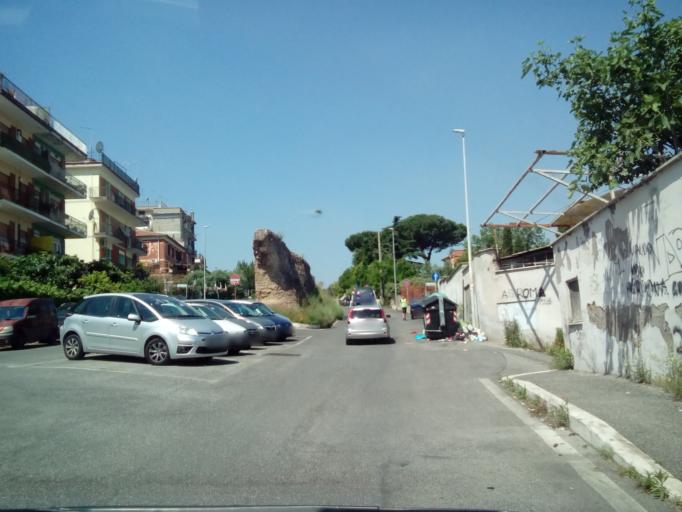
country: IT
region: Latium
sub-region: Citta metropolitana di Roma Capitale
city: Rome
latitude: 41.8794
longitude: 12.5813
